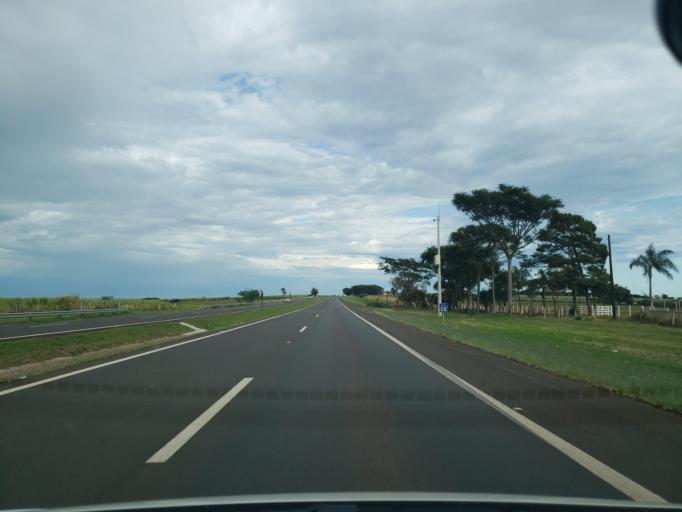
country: BR
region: Sao Paulo
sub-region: Jau
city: Jau
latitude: -22.2690
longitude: -48.4600
